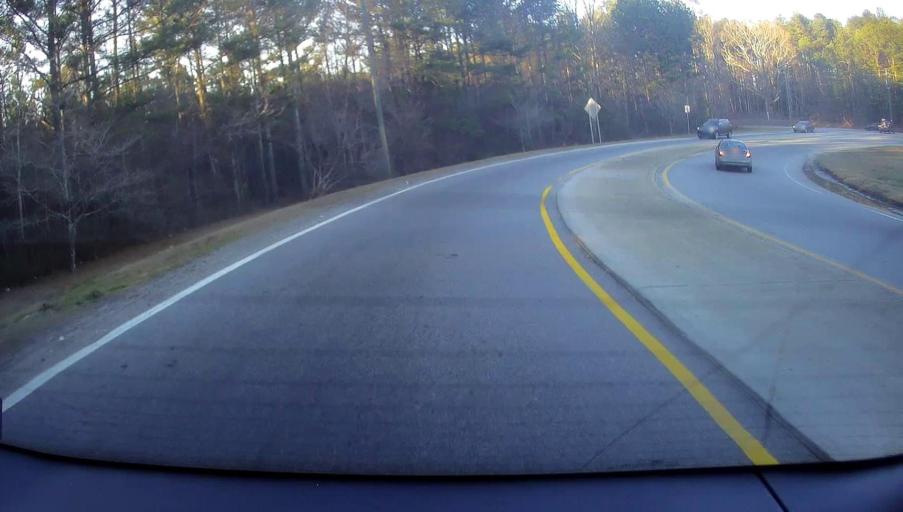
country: US
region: Georgia
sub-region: Fulton County
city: Fairburn
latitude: 33.5580
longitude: -84.5940
